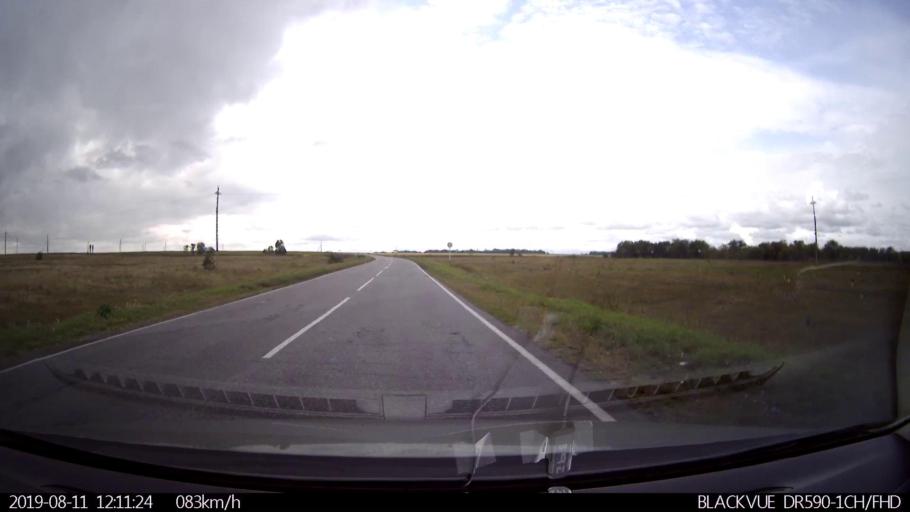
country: RU
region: Ulyanovsk
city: Silikatnyy
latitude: 53.9856
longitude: 48.0054
